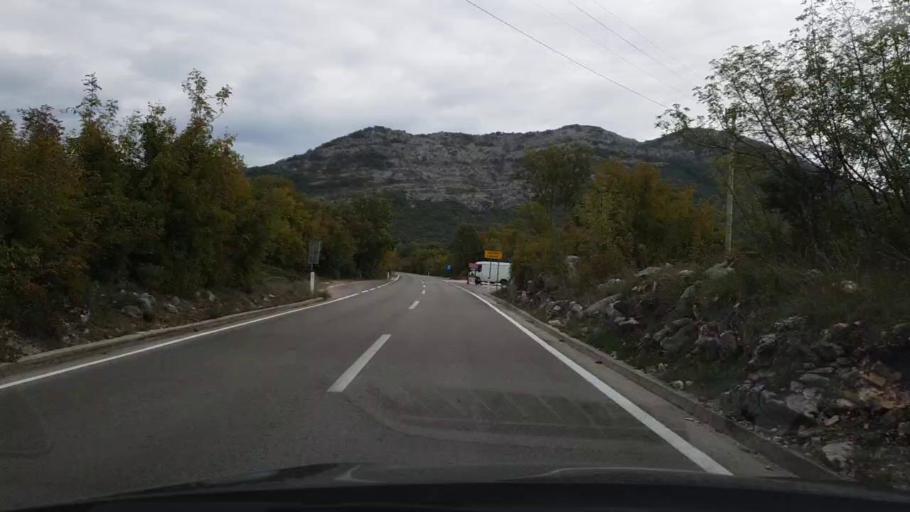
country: BA
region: Republika Srpska
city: Trebinje
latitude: 42.6888
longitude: 18.2593
